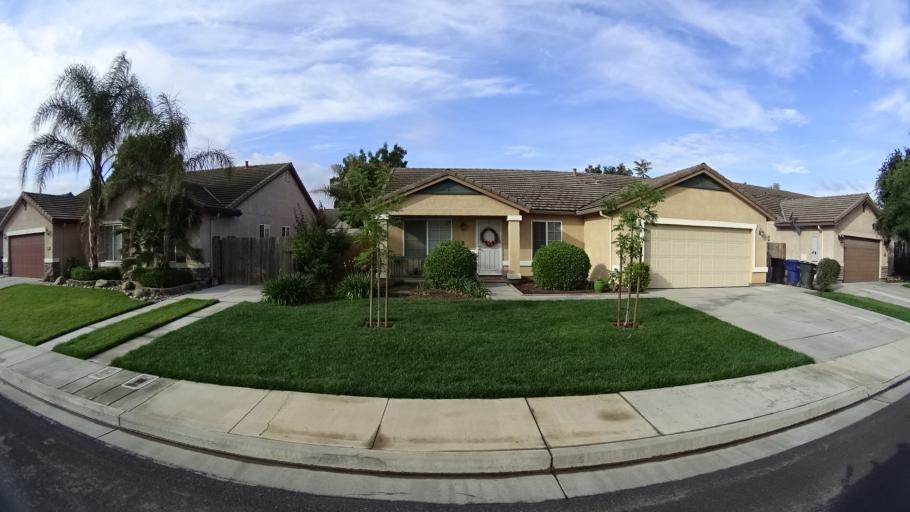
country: US
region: California
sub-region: Kings County
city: Lucerne
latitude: 36.3488
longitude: -119.6787
